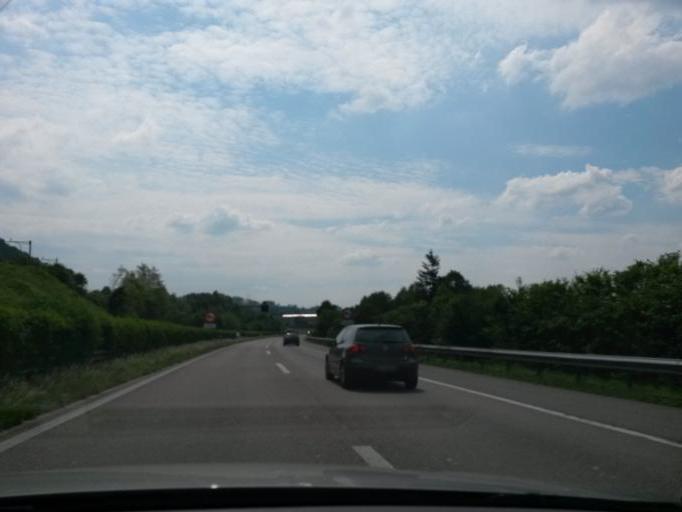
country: CH
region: Ticino
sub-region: Mendrisio District
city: Mendrisio
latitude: 45.8844
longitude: 8.9802
